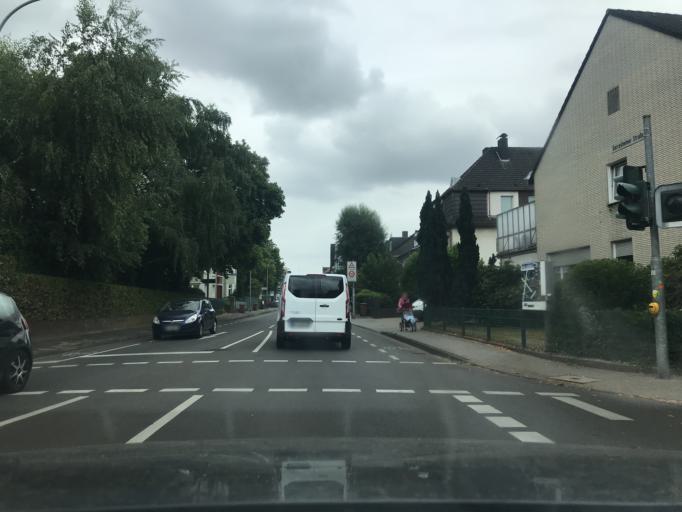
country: DE
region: North Rhine-Westphalia
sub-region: Regierungsbezirk Dusseldorf
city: Hilden
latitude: 51.1721
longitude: 6.9289
